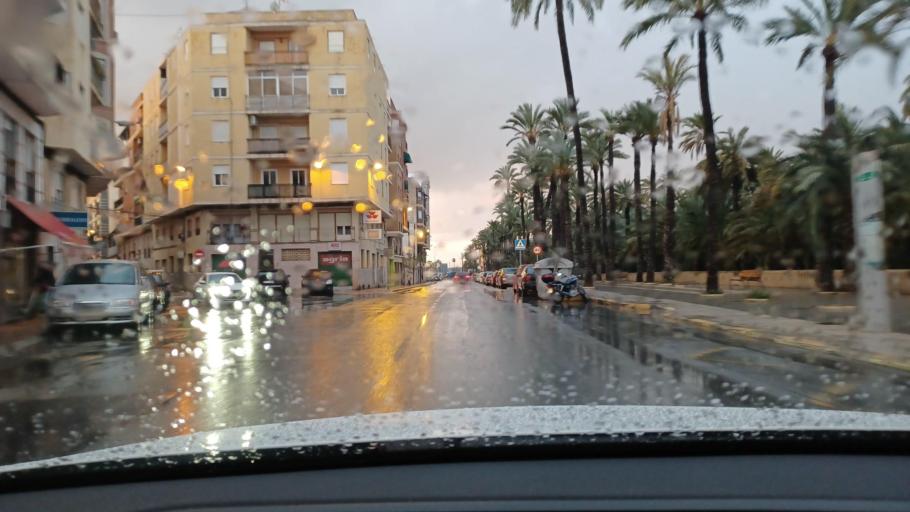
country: ES
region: Valencia
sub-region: Provincia de Alicante
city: Elche
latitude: 38.2564
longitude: -0.6972
